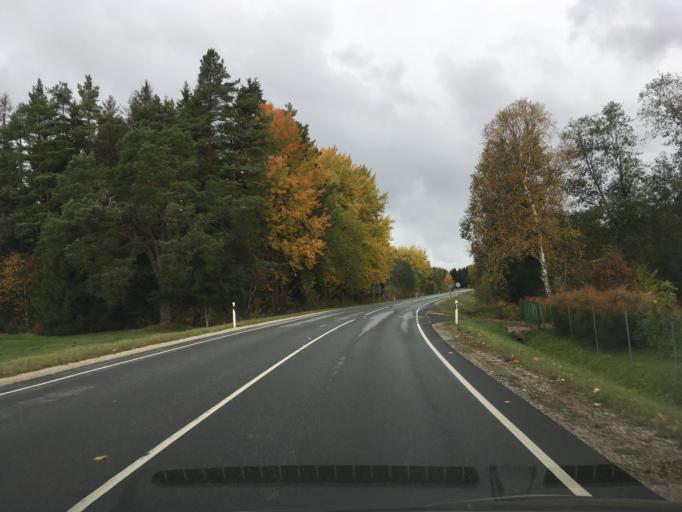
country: EE
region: Harju
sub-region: Anija vald
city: Kehra
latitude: 59.3130
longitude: 25.3437
